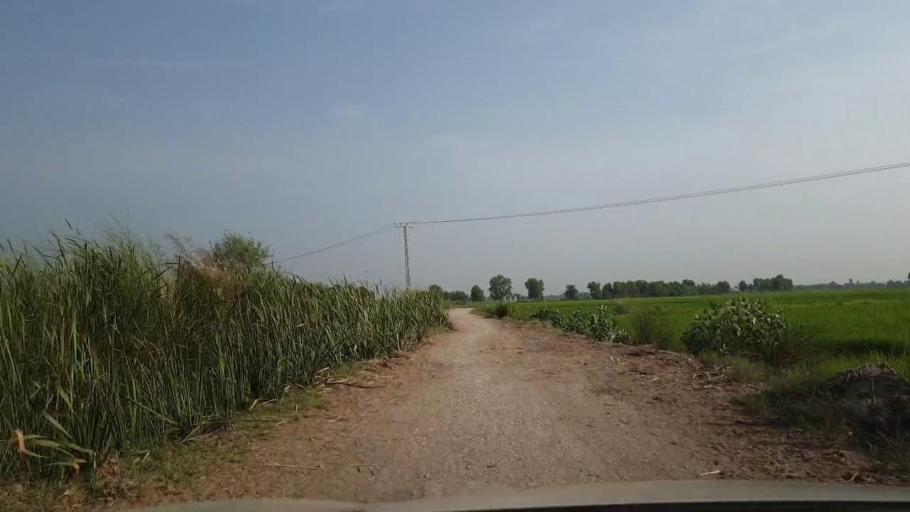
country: PK
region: Sindh
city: Larkana
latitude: 27.4891
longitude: 68.2069
